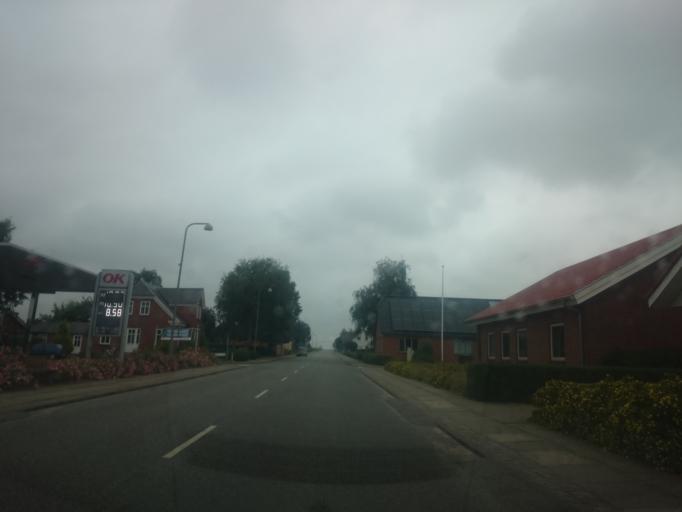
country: DK
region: South Denmark
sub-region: Vejen Kommune
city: Holsted
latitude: 55.6021
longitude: 8.8028
